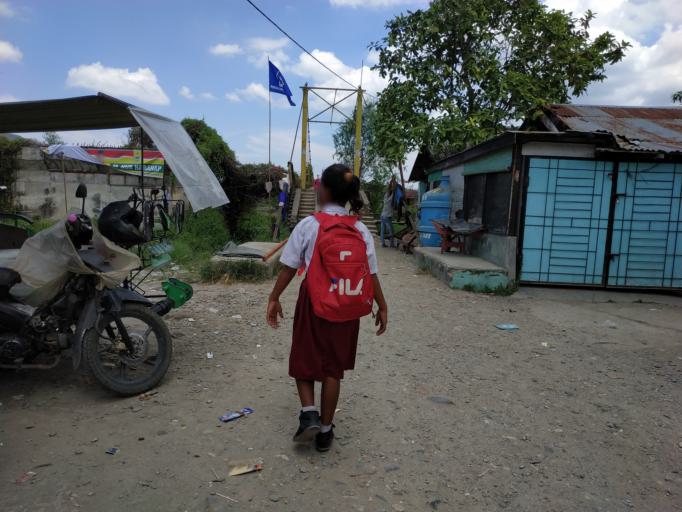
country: ID
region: North Sumatra
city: Tanjungbalai
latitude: 2.9575
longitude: 99.8169
